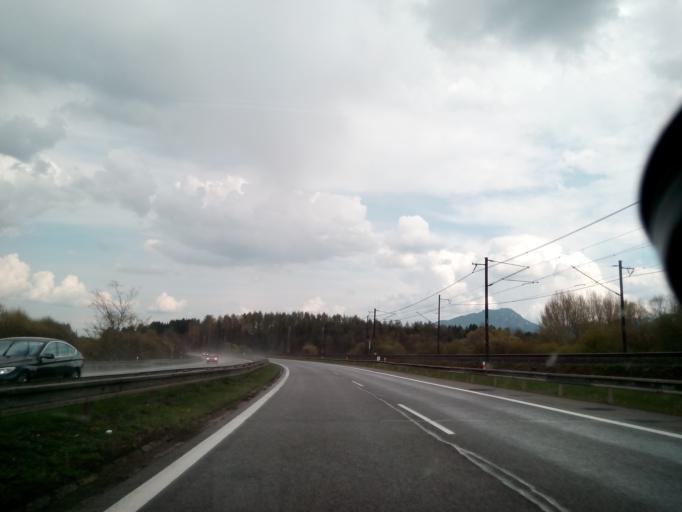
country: SK
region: Zilinsky
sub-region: Okres Liptovsky Mikulas
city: Liptovsky Mikulas
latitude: 49.0878
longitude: 19.5355
